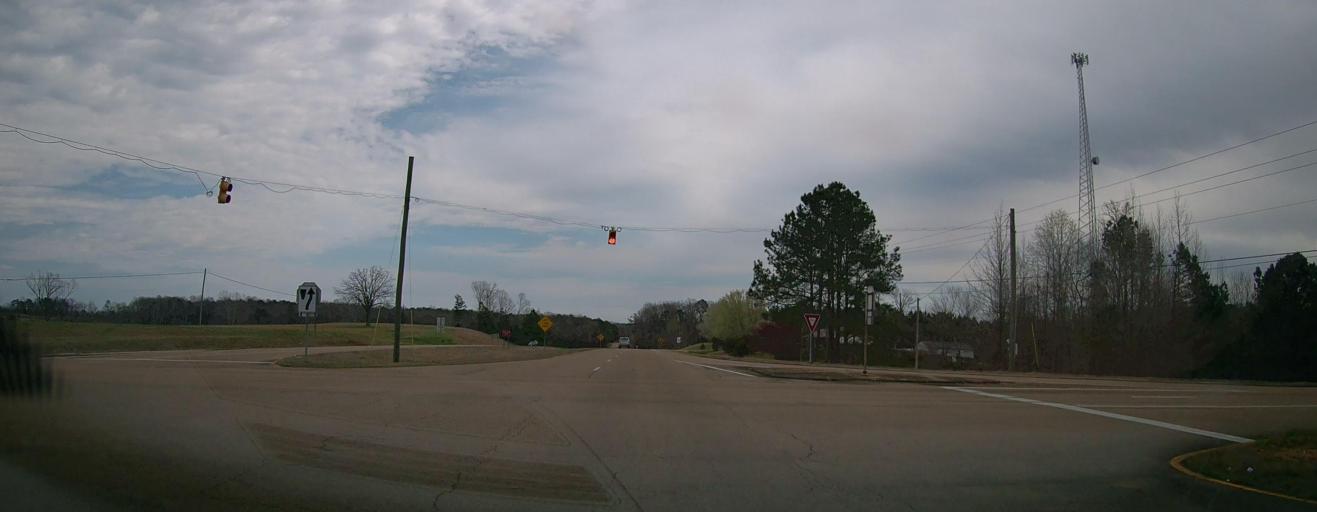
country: US
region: Mississippi
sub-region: Itawamba County
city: Fulton
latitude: 34.2655
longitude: -88.3306
